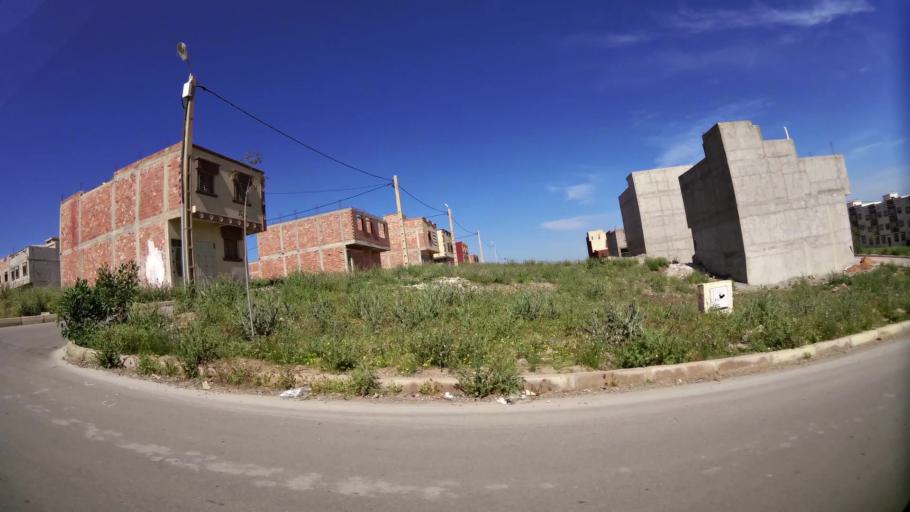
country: MA
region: Oriental
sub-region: Oujda-Angad
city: Oujda
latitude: 34.6537
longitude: -1.9417
